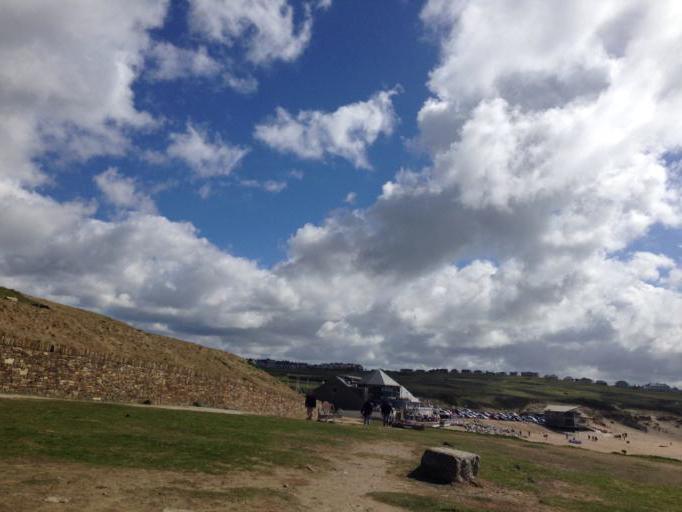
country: GB
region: England
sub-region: Cornwall
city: Newquay
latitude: 50.4205
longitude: -5.0981
